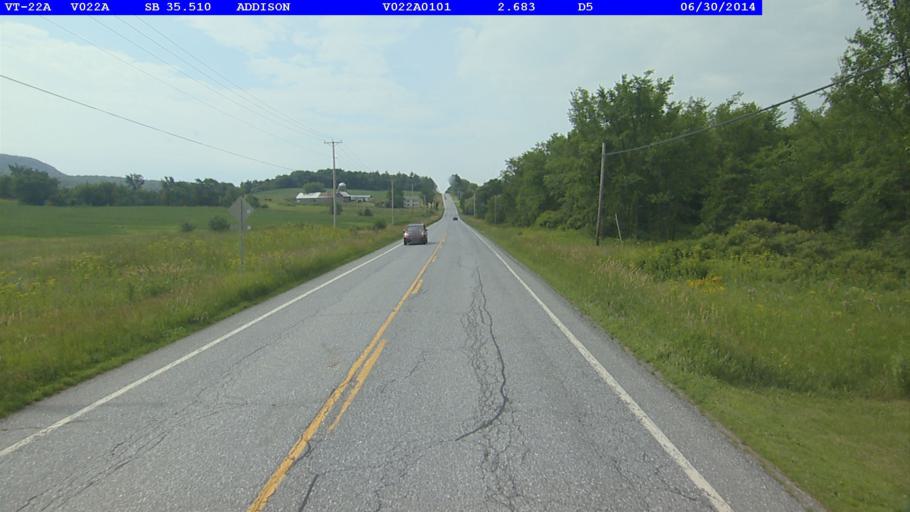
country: US
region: Vermont
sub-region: Addison County
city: Vergennes
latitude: 44.0680
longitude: -73.3043
